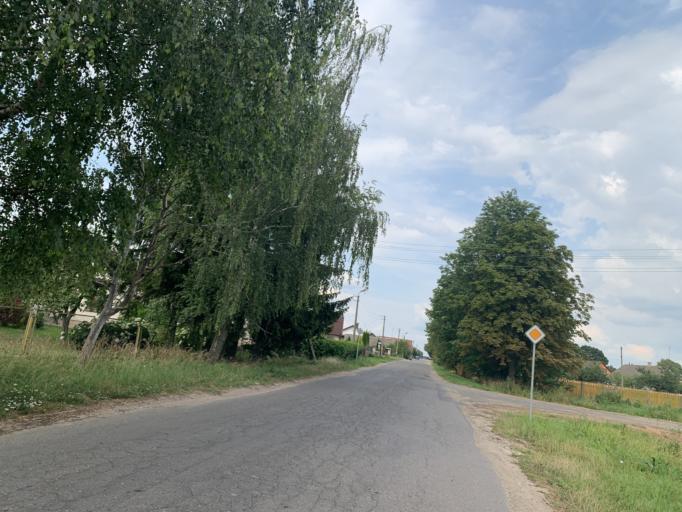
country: BY
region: Minsk
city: Nyasvizh
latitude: 53.2057
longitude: 26.6824
